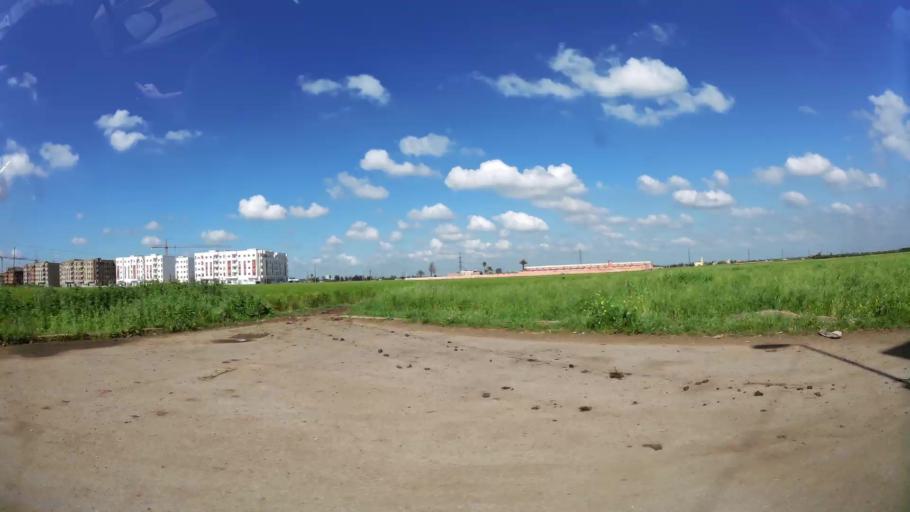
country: MA
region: Grand Casablanca
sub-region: Mediouna
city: Mediouna
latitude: 33.4588
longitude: -7.5063
